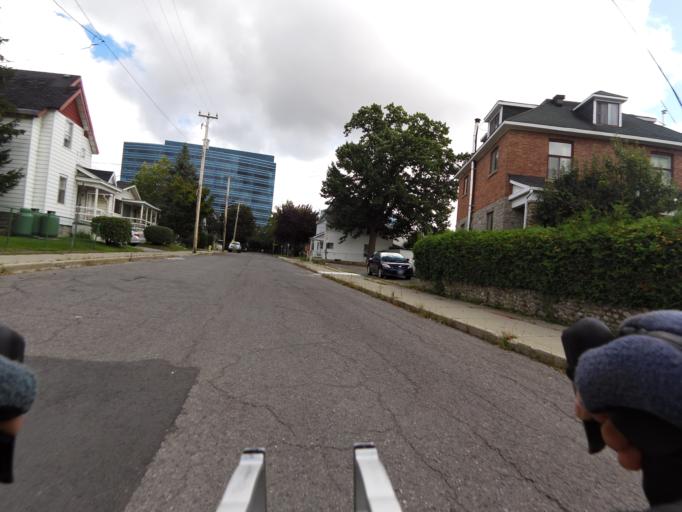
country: CA
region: Ontario
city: Ottawa
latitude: 45.4320
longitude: -75.6662
